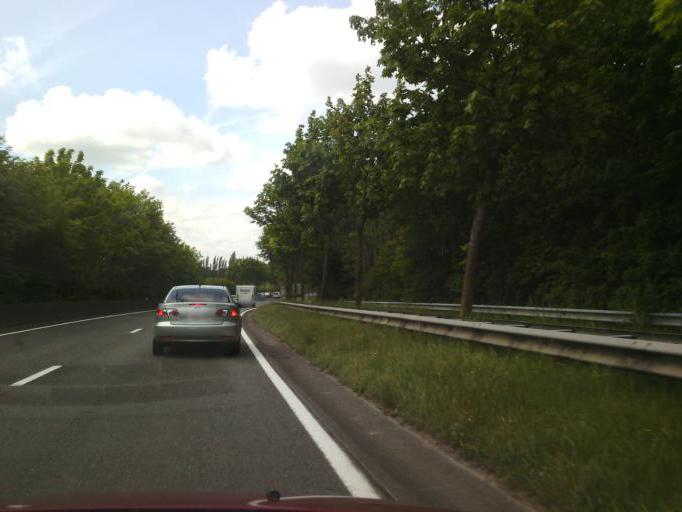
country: BE
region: Flanders
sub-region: Provincie Oost-Vlaanderen
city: Gent
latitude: 51.0375
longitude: 3.6826
